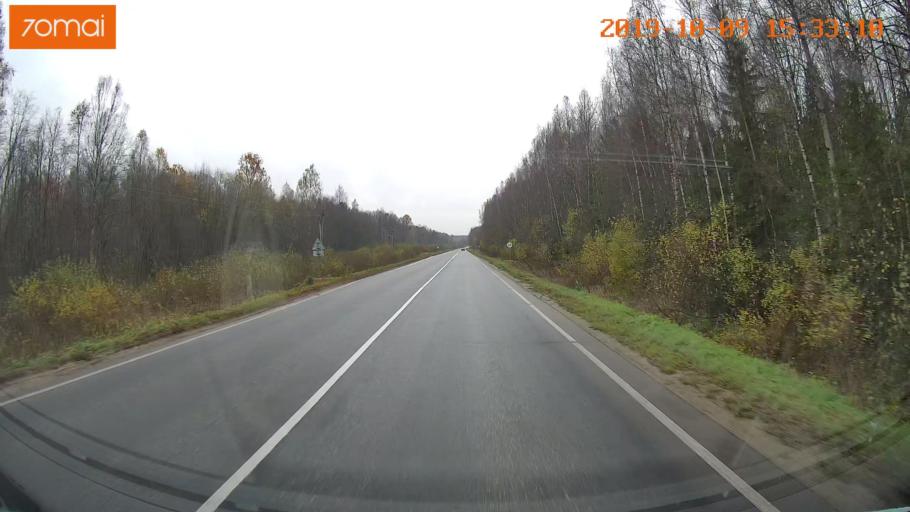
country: RU
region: Kostroma
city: Oktyabr'skiy
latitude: 57.9554
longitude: 41.2661
